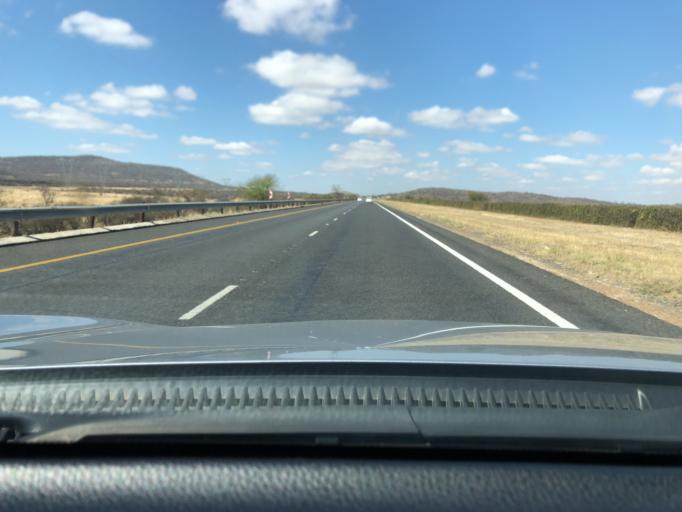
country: ZA
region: KwaZulu-Natal
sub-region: uThukela District Municipality
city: Estcourt
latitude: -28.8145
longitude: 29.6950
